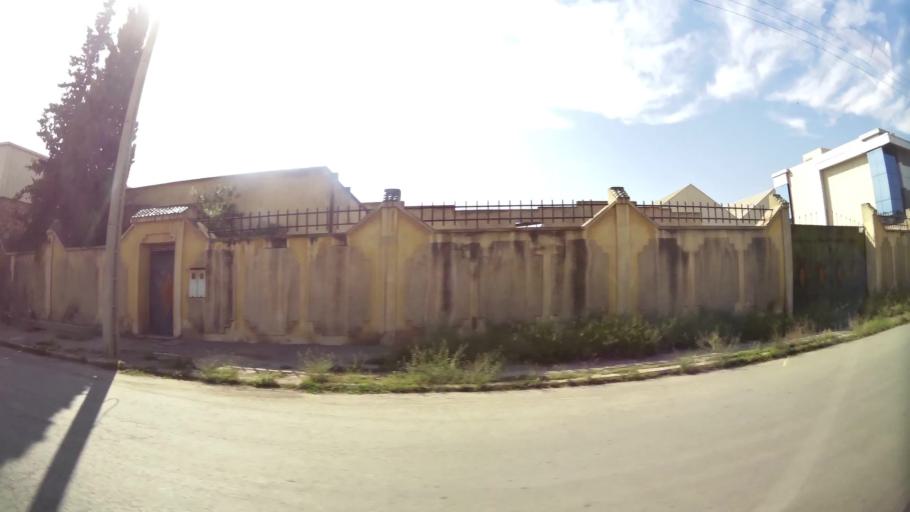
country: MA
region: Oriental
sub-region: Oujda-Angad
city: Oujda
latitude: 34.7026
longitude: -1.8917
